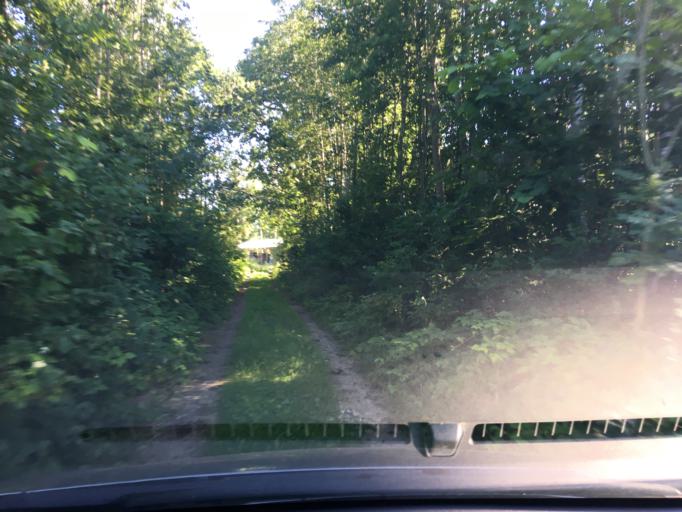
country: EE
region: Laeaene
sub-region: Lihula vald
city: Lihula
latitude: 58.5869
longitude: 23.7362
